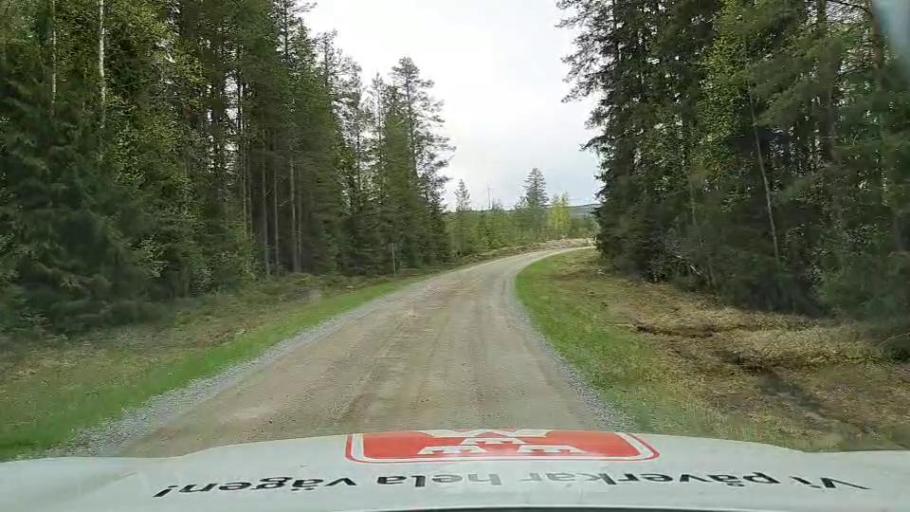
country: SE
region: Jaemtland
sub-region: Bergs Kommun
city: Hoverberg
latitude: 62.4986
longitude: 14.7068
